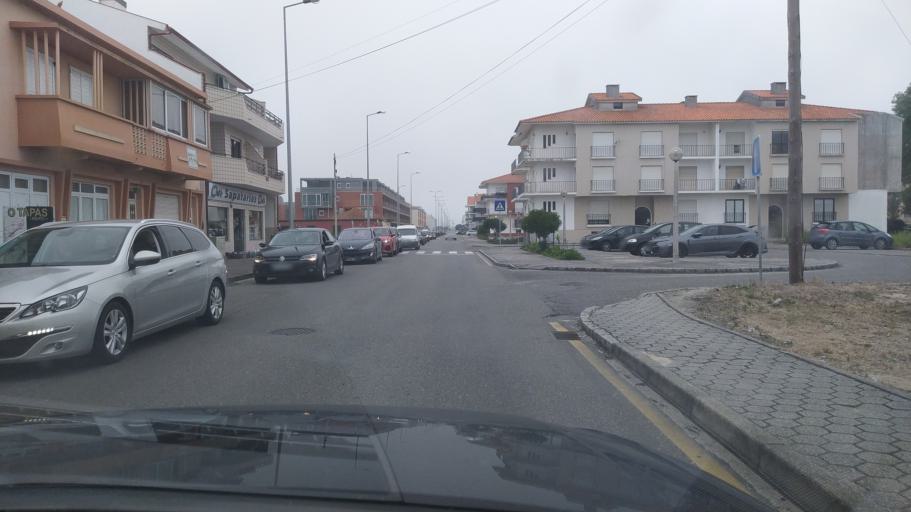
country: PT
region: Aveiro
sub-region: Ilhavo
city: Gafanha da Encarnacao
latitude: 40.5608
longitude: -8.7591
